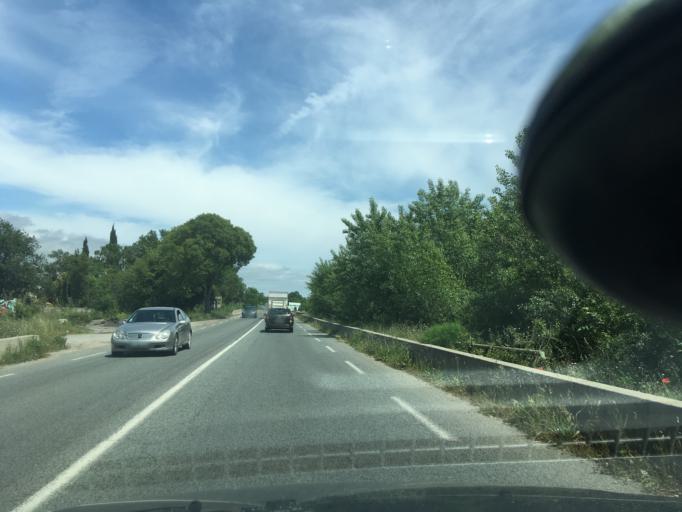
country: FR
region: Provence-Alpes-Cote d'Azur
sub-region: Departement du Var
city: Roquebrune-sur-Argens
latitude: 43.4622
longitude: 6.6466
